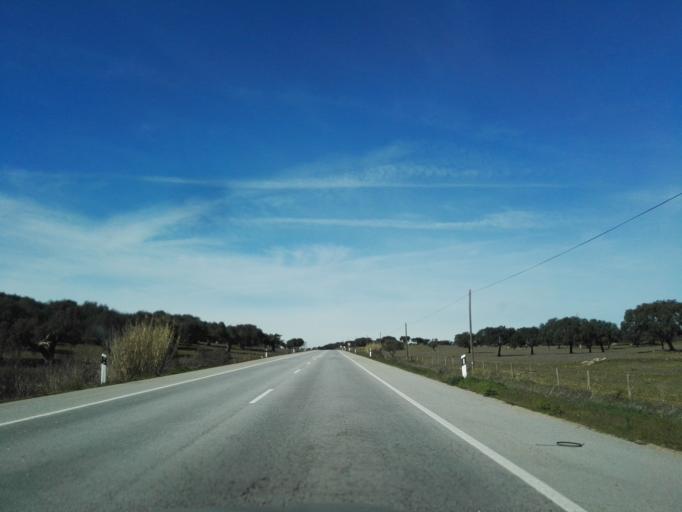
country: PT
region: Portalegre
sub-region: Arronches
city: Arronches
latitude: 39.1706
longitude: -7.3323
